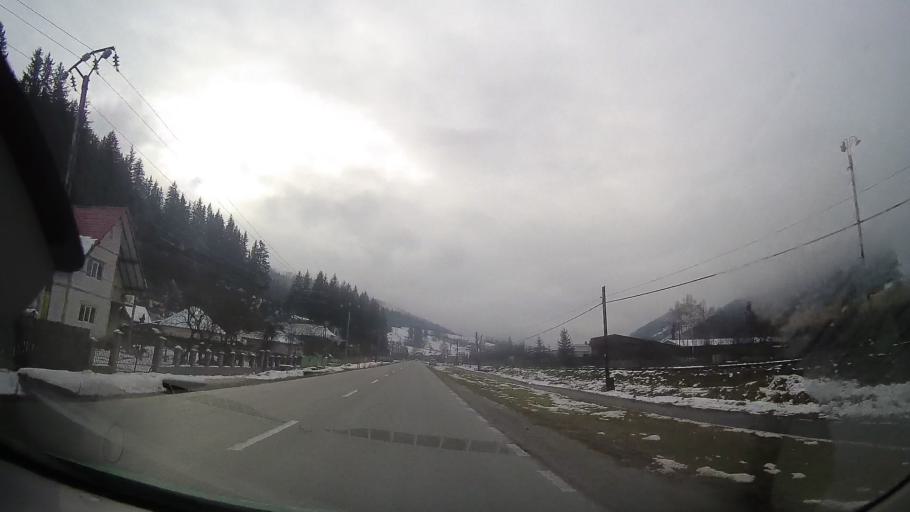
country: RO
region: Neamt
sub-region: Comuna Tasca
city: Tasca
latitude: 46.8917
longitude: 26.0178
